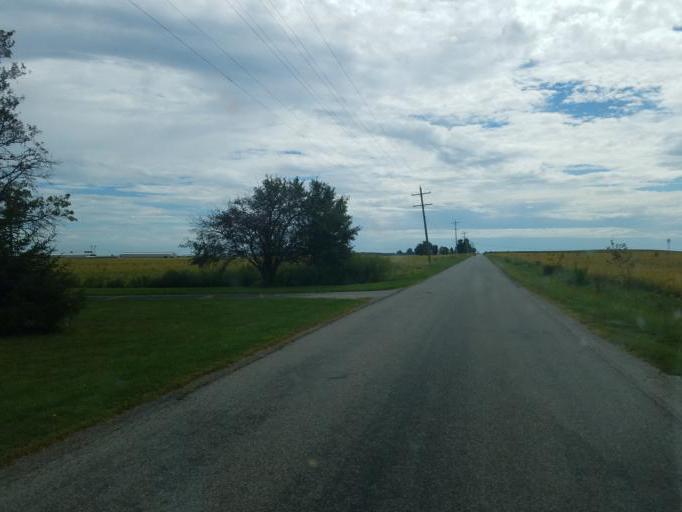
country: US
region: Ohio
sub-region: Licking County
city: Johnstown
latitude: 40.2192
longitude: -82.7150
